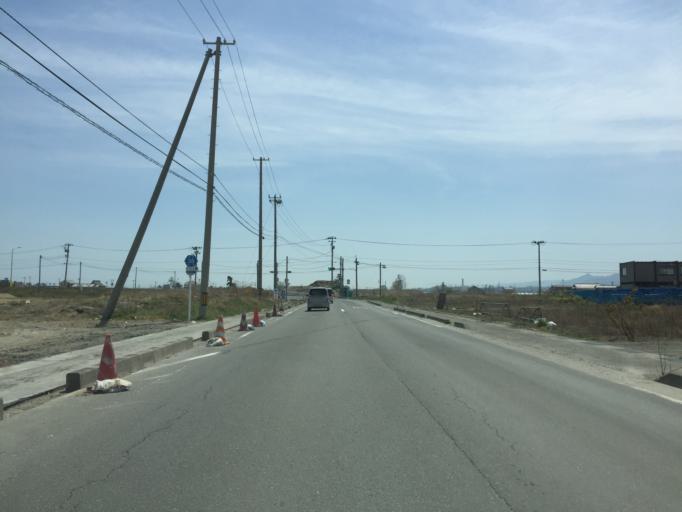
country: JP
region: Miyagi
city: Watari
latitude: 37.9740
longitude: 140.9039
